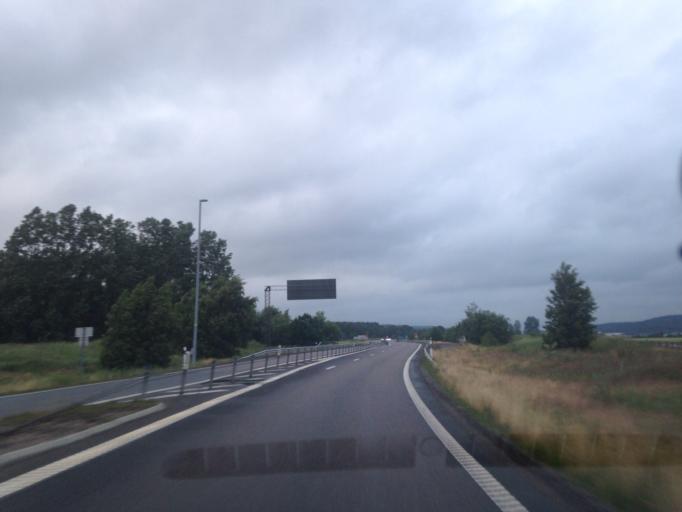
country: SE
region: Halland
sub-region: Varbergs Kommun
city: Varberg
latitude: 57.1460
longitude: 12.2687
